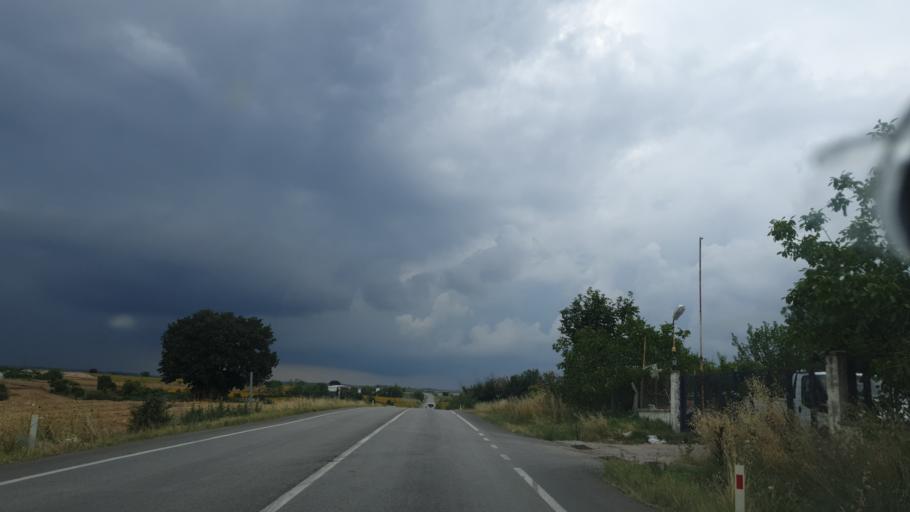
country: TR
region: Tekirdag
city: Hayrabolu
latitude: 41.2190
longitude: 27.0787
